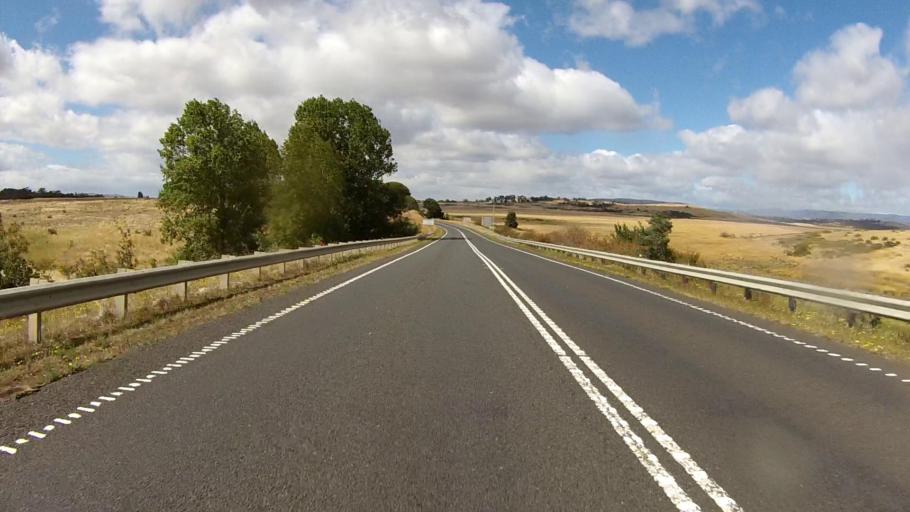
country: AU
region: Tasmania
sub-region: Northern Midlands
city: Evandale
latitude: -41.8413
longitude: 147.4482
